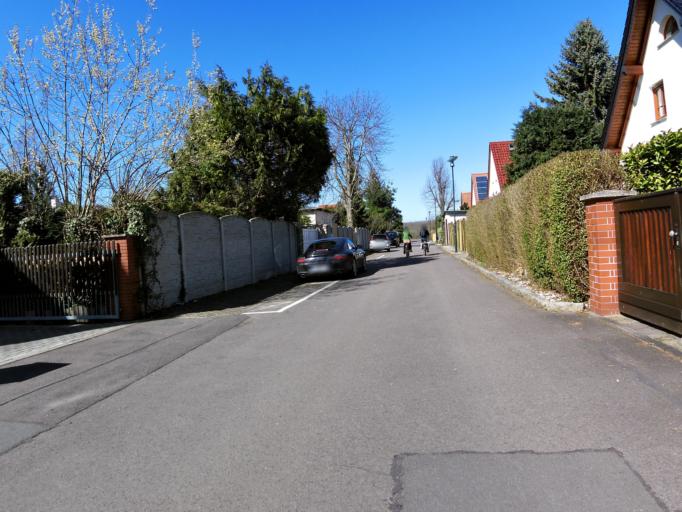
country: DE
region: Saxony
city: Markkleeberg
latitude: 51.2743
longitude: 12.4111
